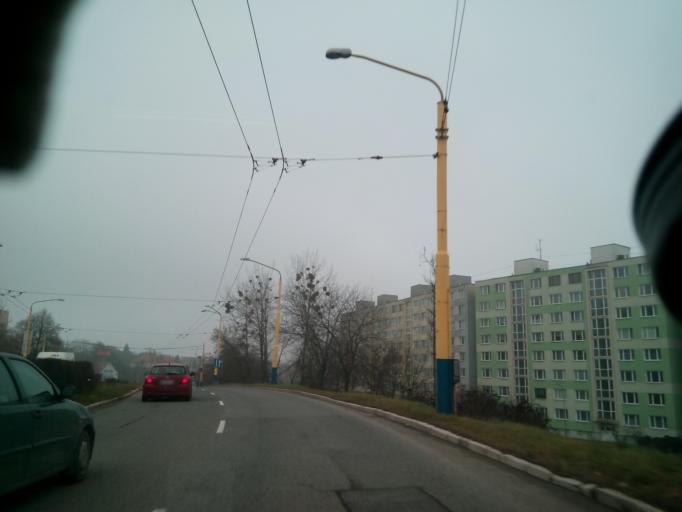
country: SK
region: Kosicky
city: Kosice
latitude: 48.7330
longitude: 21.2860
